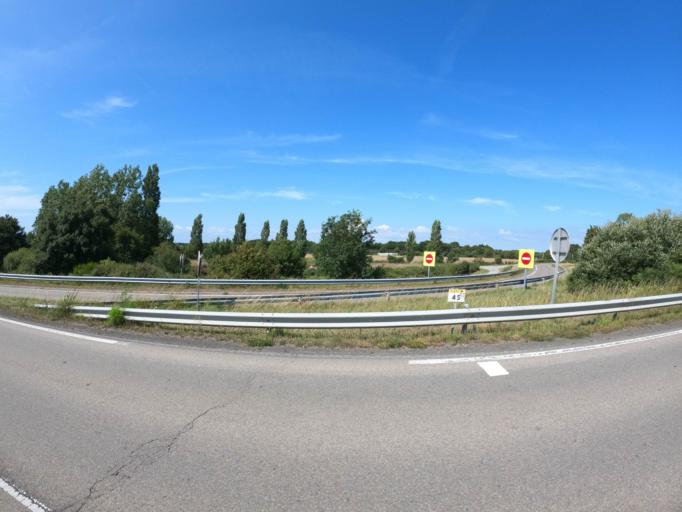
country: FR
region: Pays de la Loire
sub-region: Departement de la Loire-Atlantique
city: La Bernerie-en-Retz
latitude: 47.1052
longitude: -2.0518
